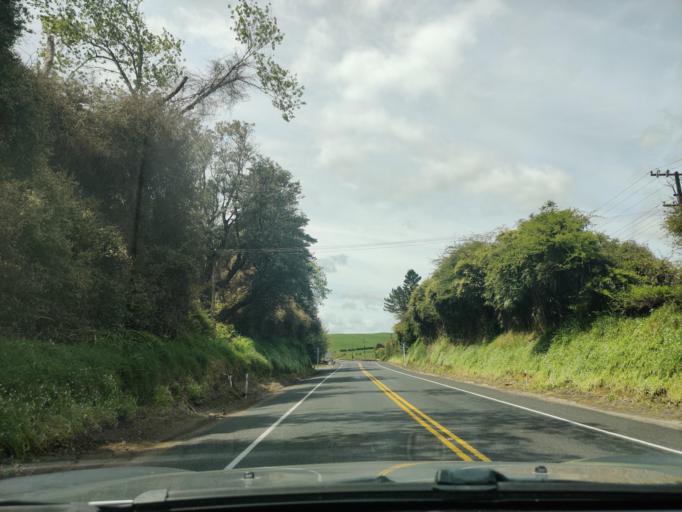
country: NZ
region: Taranaki
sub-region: New Plymouth District
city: New Plymouth
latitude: -39.1482
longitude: 174.1495
